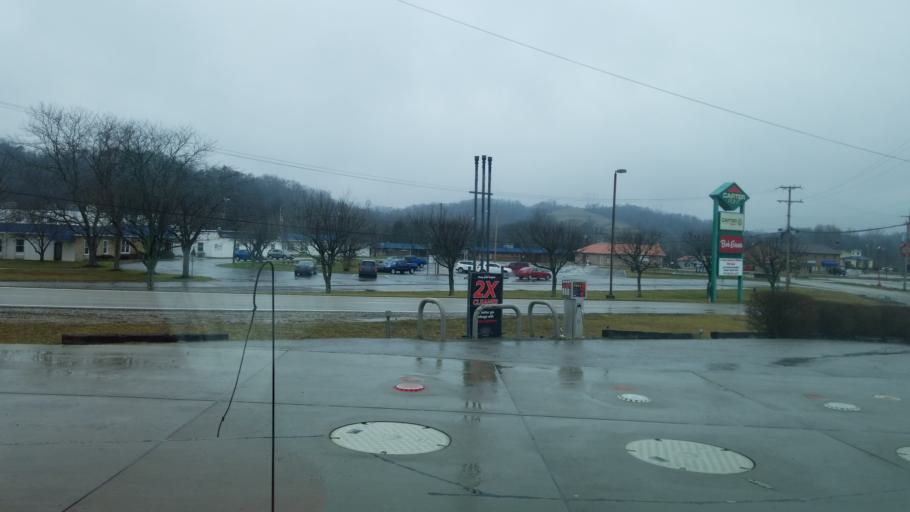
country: US
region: West Virginia
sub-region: Jackson County
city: Ripley
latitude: 38.8221
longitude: -81.7288
